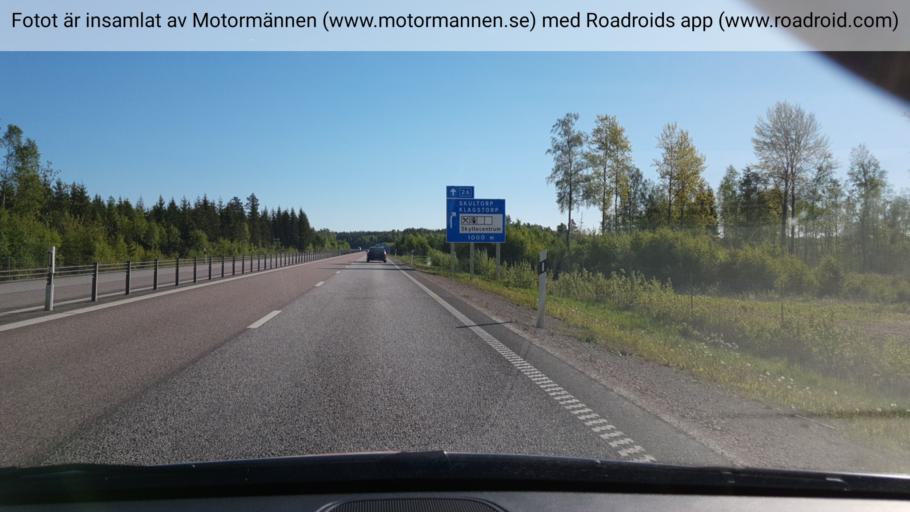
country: SE
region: Vaestra Goetaland
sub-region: Skovde Kommun
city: Skultorp
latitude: 58.3308
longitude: 13.8507
